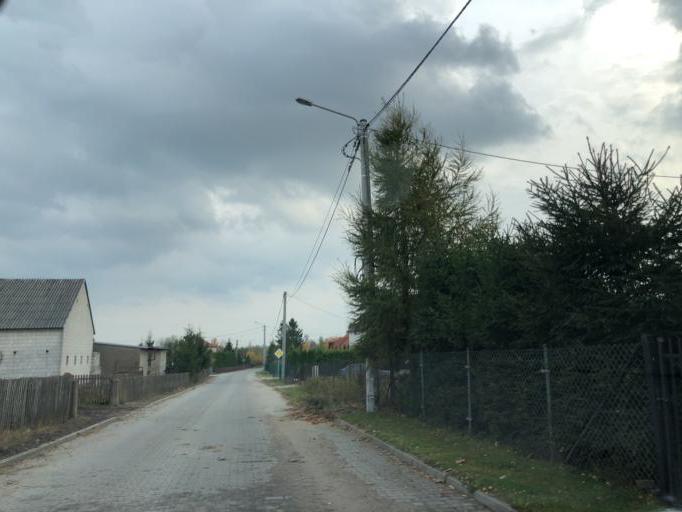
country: PL
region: Podlasie
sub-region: Lomza
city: Lomza
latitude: 53.1229
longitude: 22.0090
